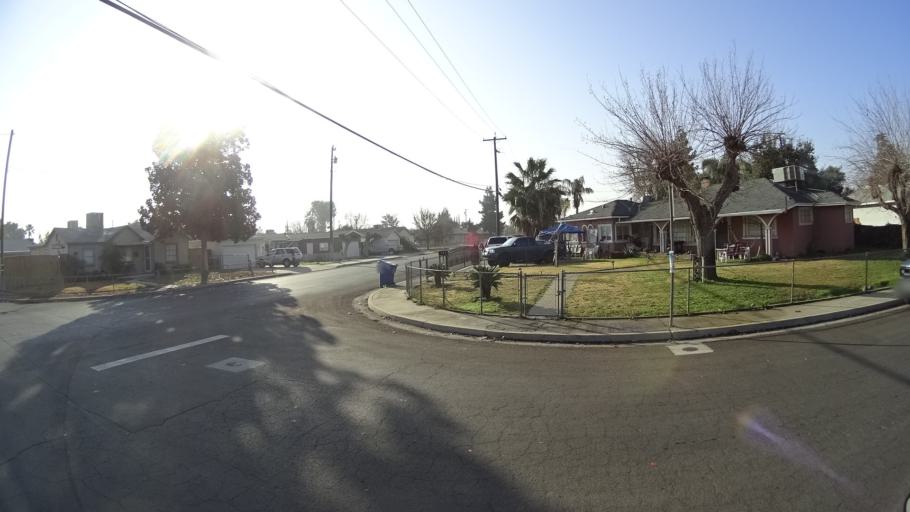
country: US
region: California
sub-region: Kern County
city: Bakersfield
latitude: 35.3532
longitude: -119.0524
